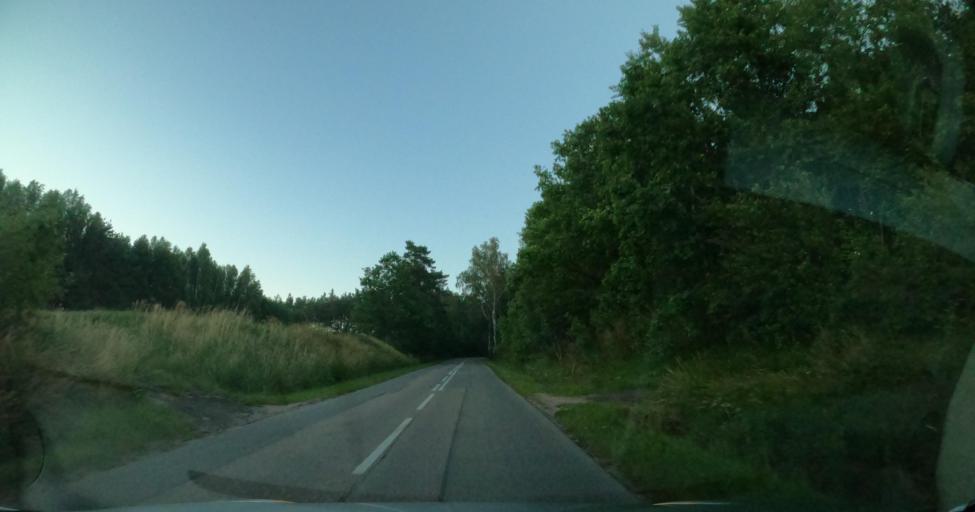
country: PL
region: Pomeranian Voivodeship
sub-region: Powiat wejherowski
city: Linia
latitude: 54.4648
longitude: 17.9835
